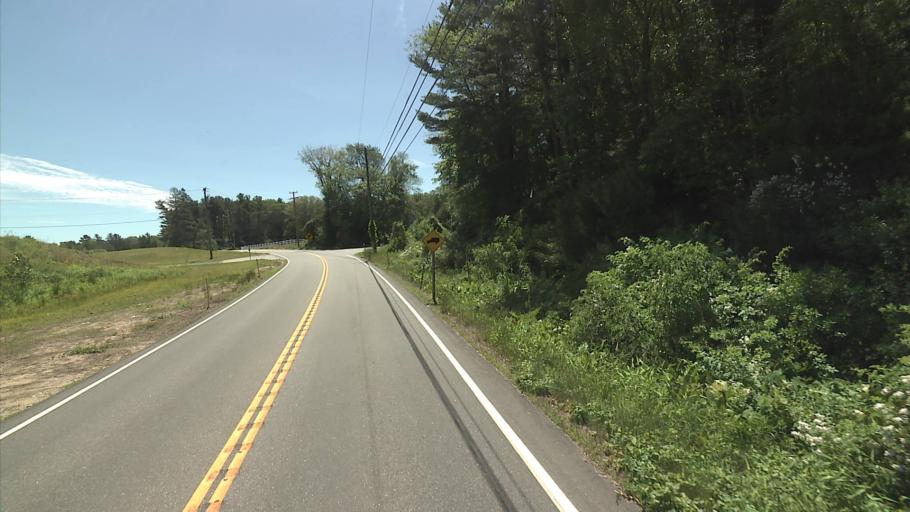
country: US
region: Rhode Island
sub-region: Washington County
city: Hopkinton
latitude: 41.5509
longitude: -71.8486
